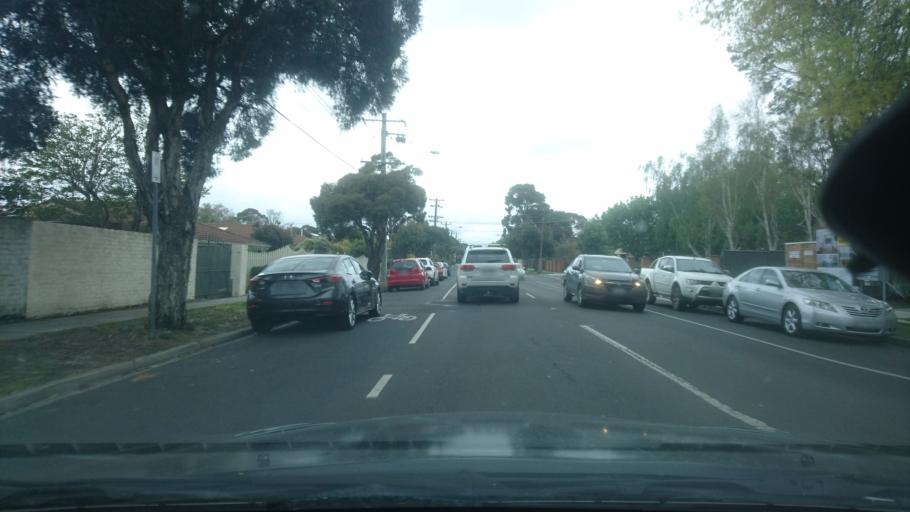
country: AU
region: Victoria
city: Carnegie
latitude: -37.8857
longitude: 145.0673
